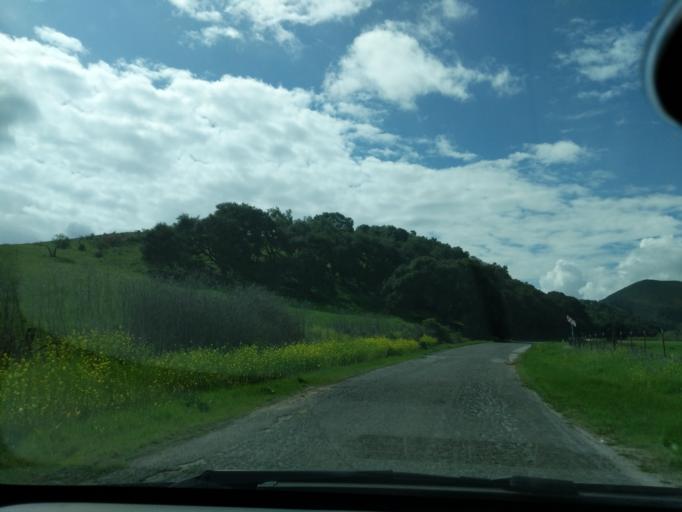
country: US
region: California
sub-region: San Benito County
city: San Juan Bautista
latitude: 36.7867
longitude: -121.5807
